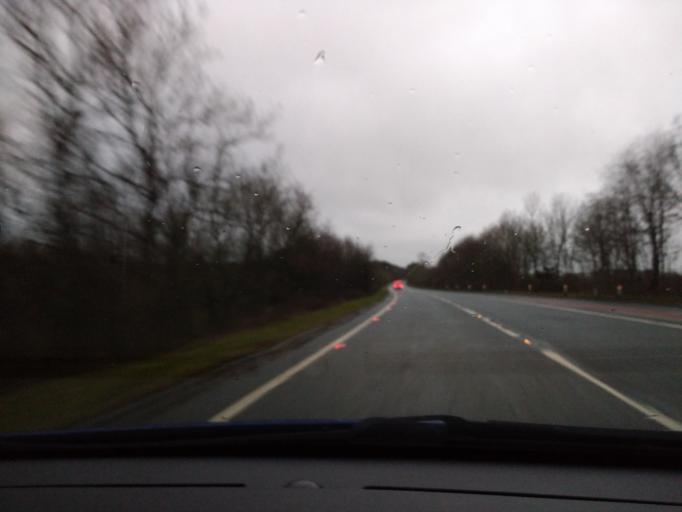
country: GB
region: England
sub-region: Cumbria
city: Cockermouth
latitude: 54.6578
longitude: -3.3237
